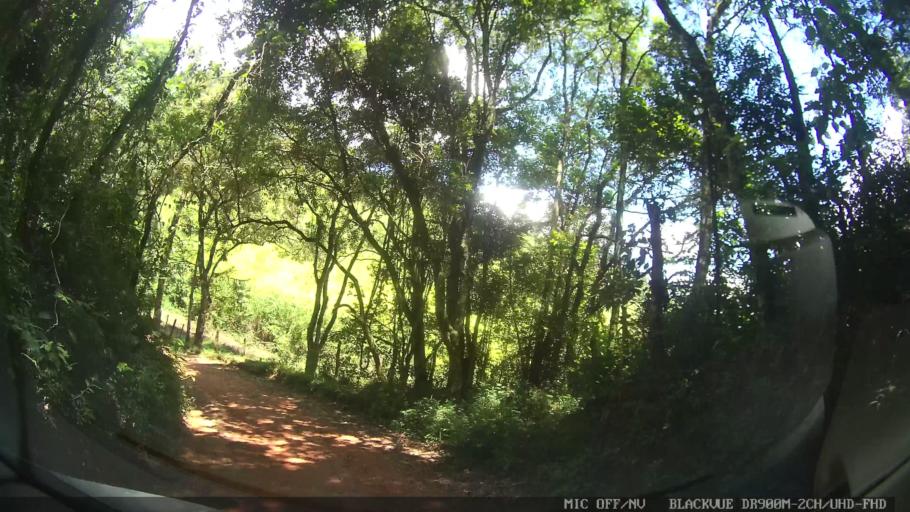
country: BR
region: Minas Gerais
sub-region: Extrema
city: Extrema
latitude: -22.8917
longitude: -46.3033
